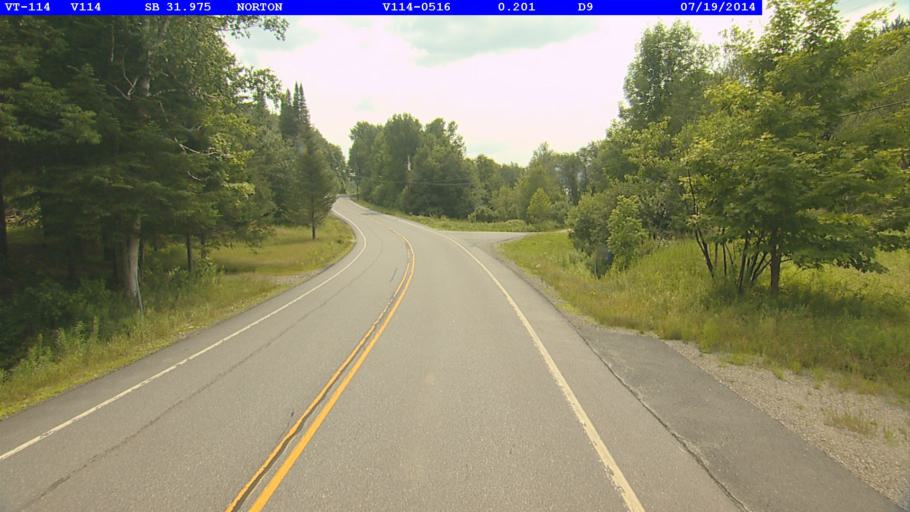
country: CA
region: Quebec
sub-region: Estrie
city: Coaticook
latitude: 44.9484
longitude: -71.8456
